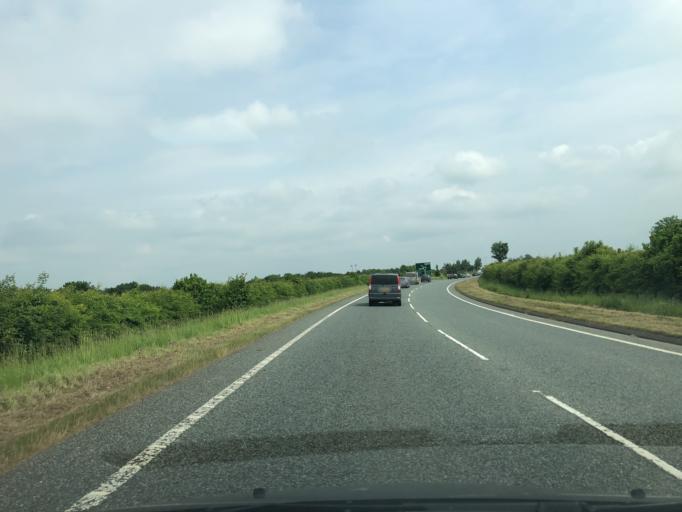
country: GB
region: England
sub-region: North Yorkshire
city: Boroughbridge
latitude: 54.1507
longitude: -1.4323
